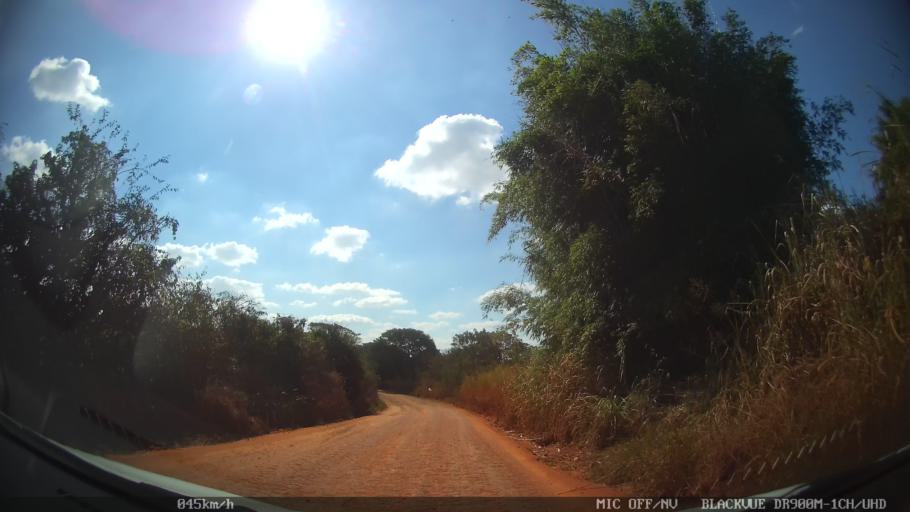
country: BR
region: Sao Paulo
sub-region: Sumare
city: Sumare
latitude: -22.8531
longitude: -47.2924
